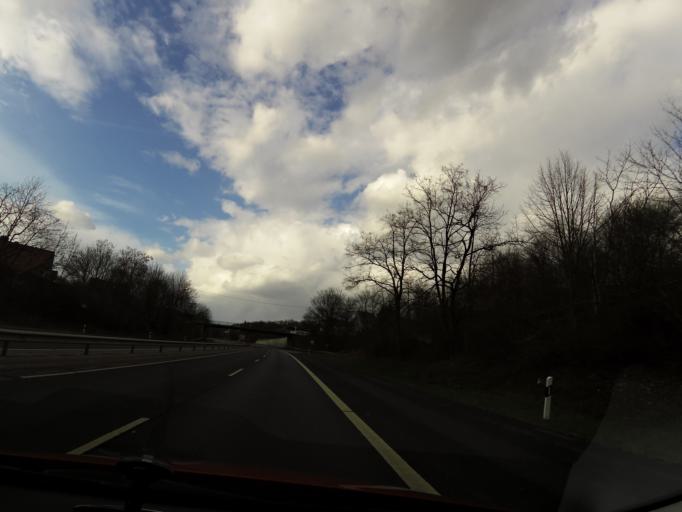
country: DE
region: Rheinland-Pfalz
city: Lahnstein
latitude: 50.3303
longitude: 7.6060
